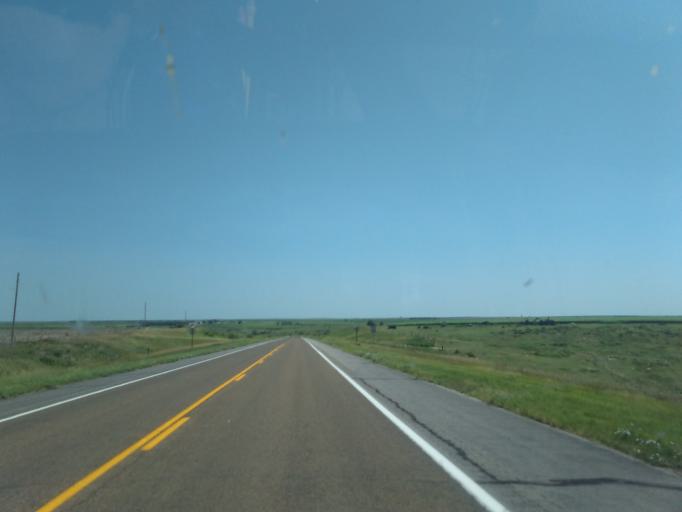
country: US
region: Nebraska
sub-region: Hitchcock County
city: Trenton
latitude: 40.1713
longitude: -101.1469
